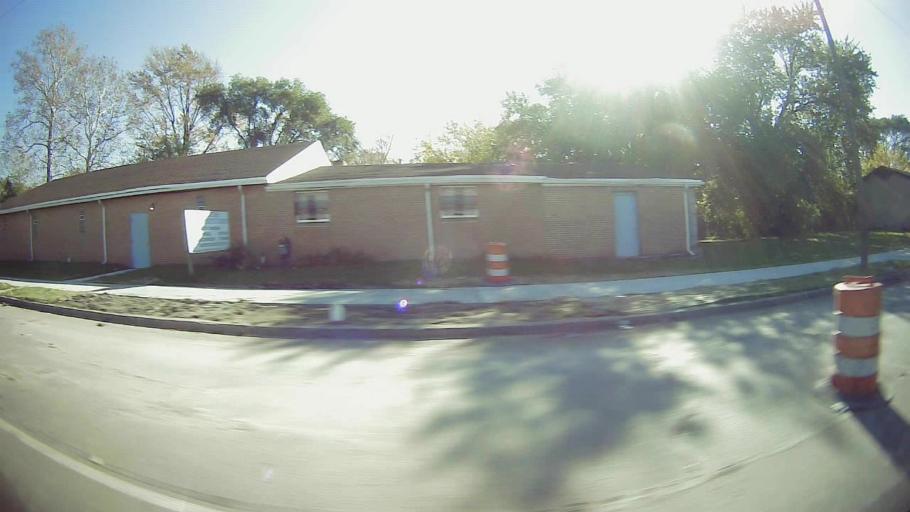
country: US
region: Michigan
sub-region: Wayne County
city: Highland Park
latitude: 42.3871
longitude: -83.1377
